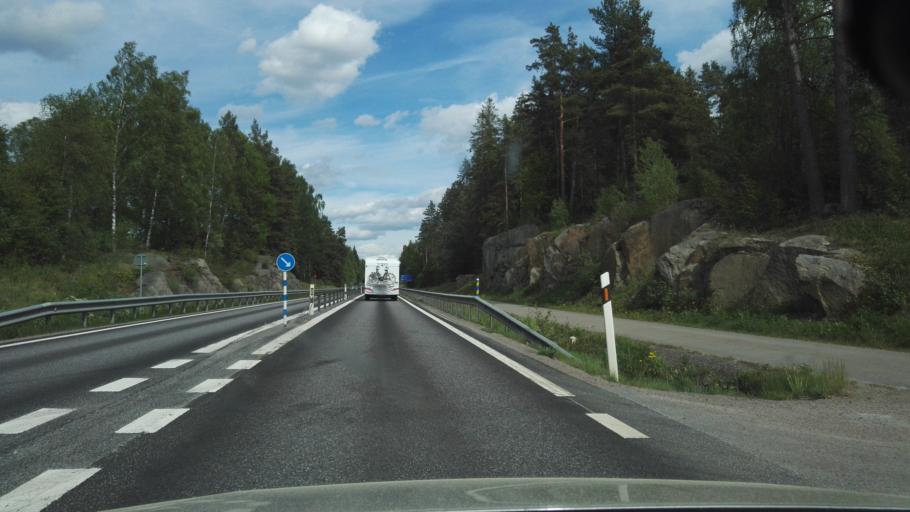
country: SE
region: Kronoberg
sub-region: Vaxjo Kommun
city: Rottne
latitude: 56.9418
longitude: 14.8869
